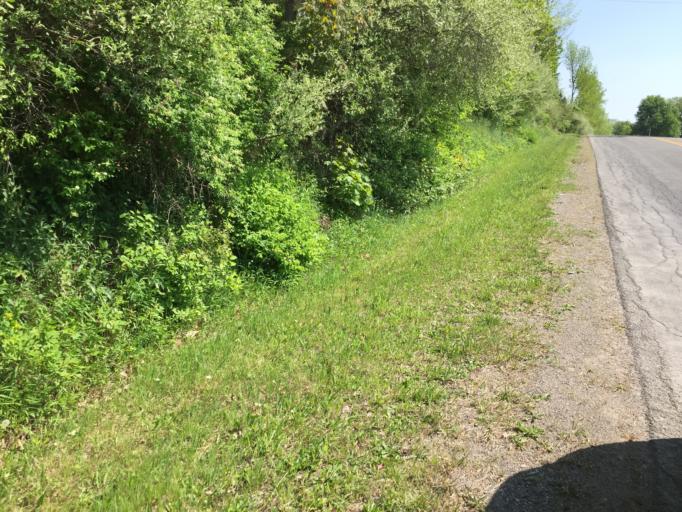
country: US
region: New York
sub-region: Wayne County
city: Marion
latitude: 43.1305
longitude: -77.1738
